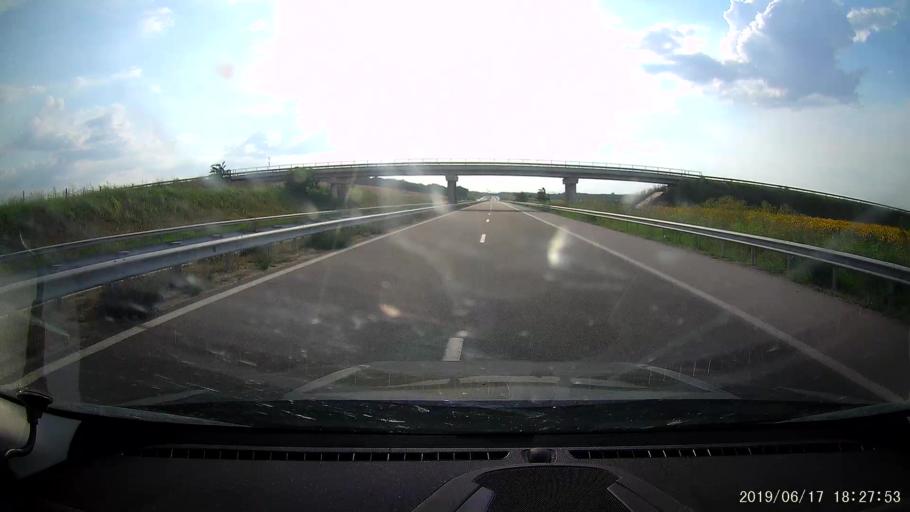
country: BG
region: Khaskovo
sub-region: Obshtina Dimitrovgrad
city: Dimitrovgrad
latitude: 42.0195
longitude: 25.5962
